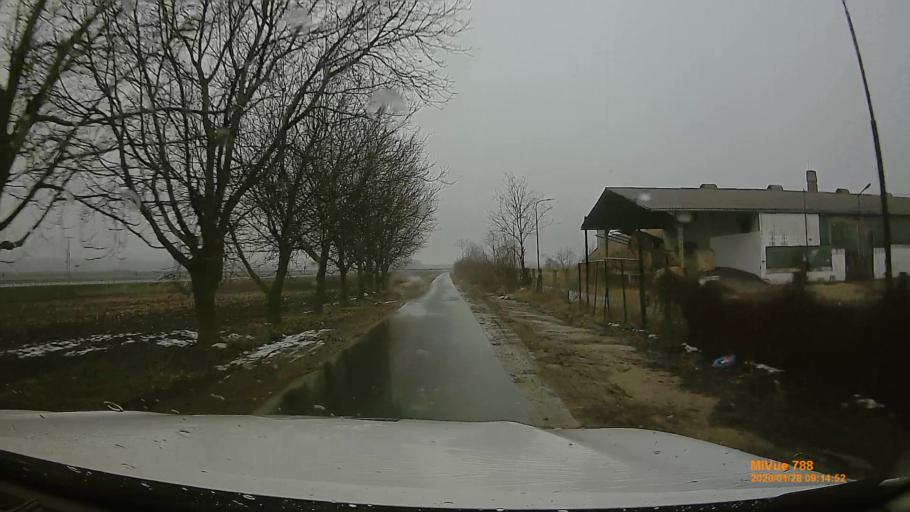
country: HU
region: Pest
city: Pilis
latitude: 47.3005
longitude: 19.5671
